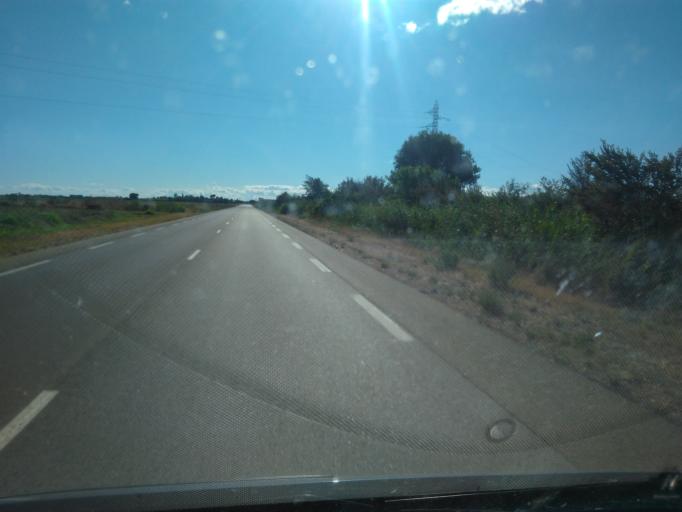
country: FR
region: Languedoc-Roussillon
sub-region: Departement du Gard
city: Bellegarde
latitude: 43.6817
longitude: 4.5261
